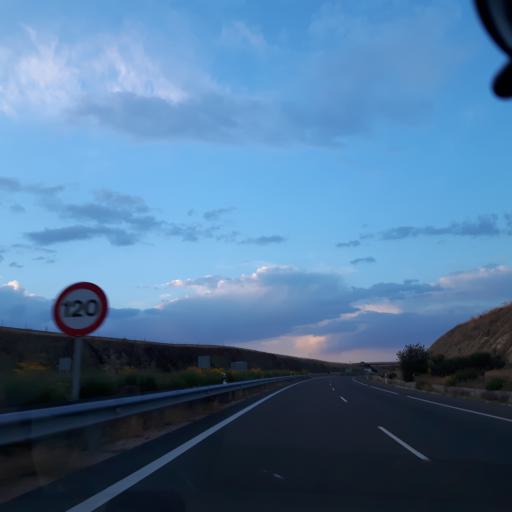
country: ES
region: Castille and Leon
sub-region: Provincia de Salamanca
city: Mozarbez
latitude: 40.8642
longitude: -5.6463
